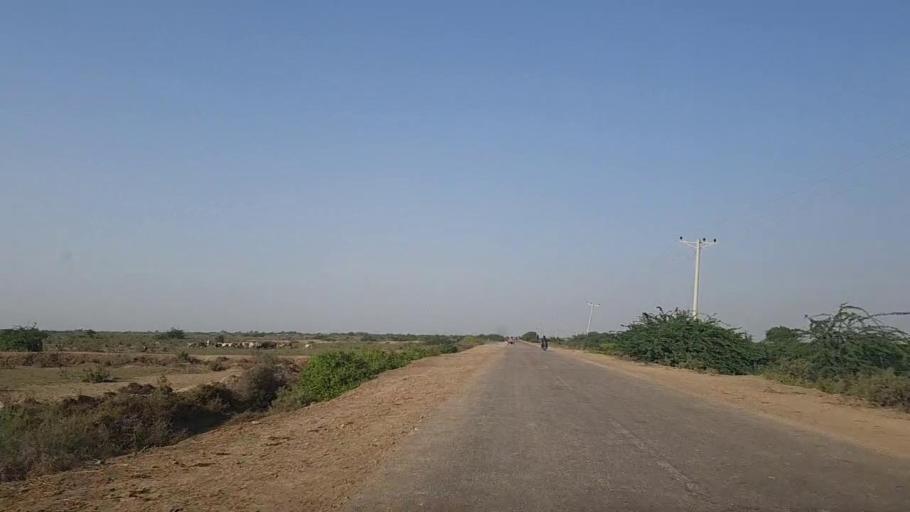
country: PK
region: Sindh
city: Mirpur Batoro
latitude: 24.6059
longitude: 68.4021
